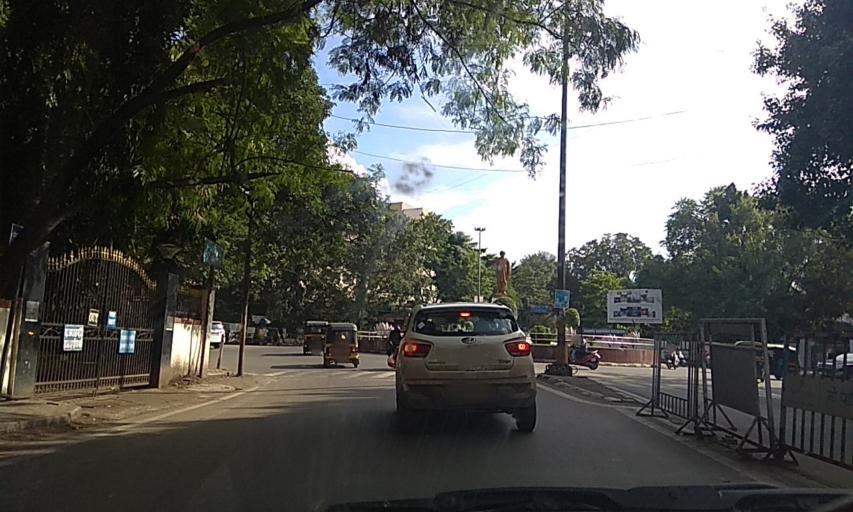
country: IN
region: Maharashtra
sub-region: Pune Division
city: Pune
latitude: 18.5253
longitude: 73.8767
